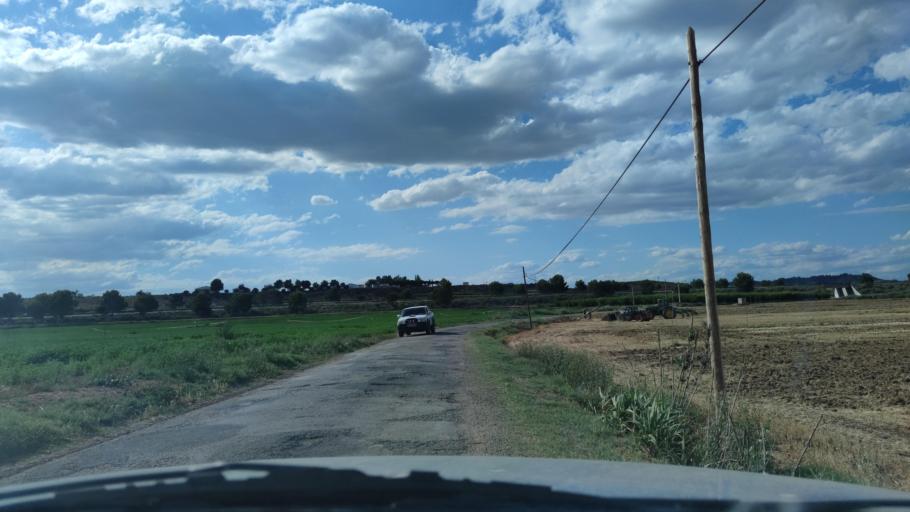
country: ES
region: Catalonia
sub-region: Provincia de Lleida
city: Alcarras
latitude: 41.5991
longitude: 0.5291
